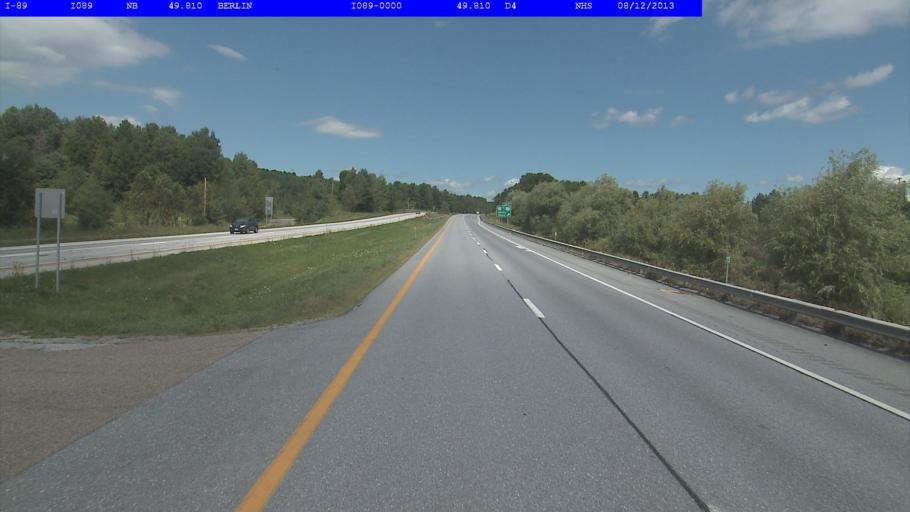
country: US
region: Vermont
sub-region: Washington County
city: Montpelier
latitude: 44.2090
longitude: -72.5814
